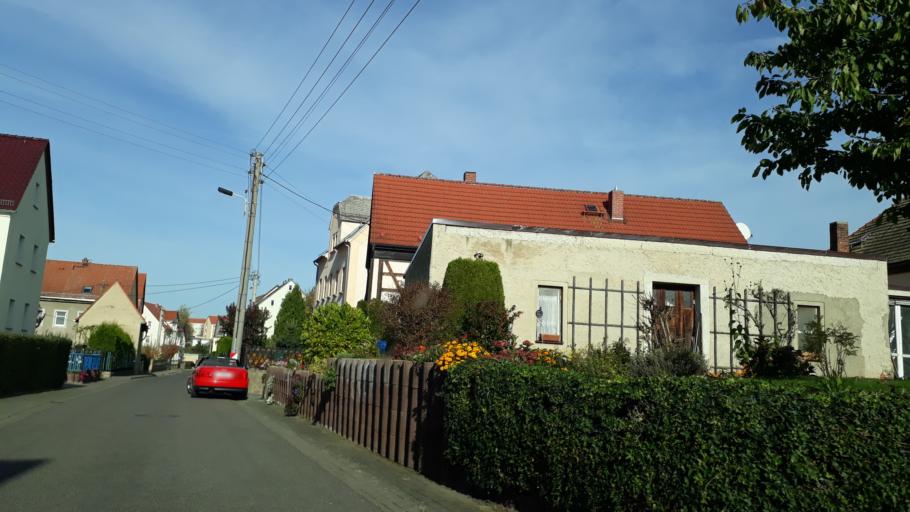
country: DE
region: Saxony
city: Dobeln
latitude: 51.1156
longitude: 13.1358
